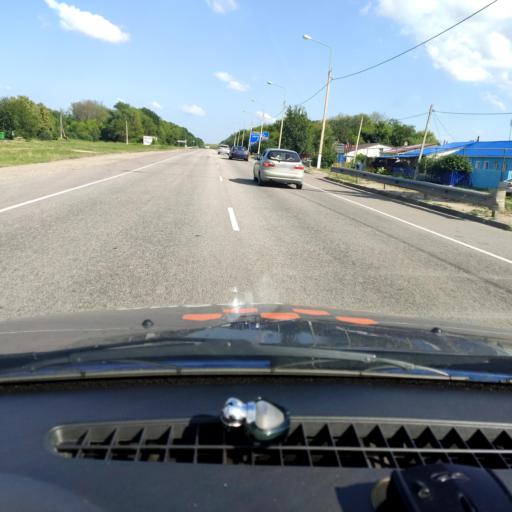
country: RU
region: Lipetsk
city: Yelets
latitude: 52.5521
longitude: 38.7070
